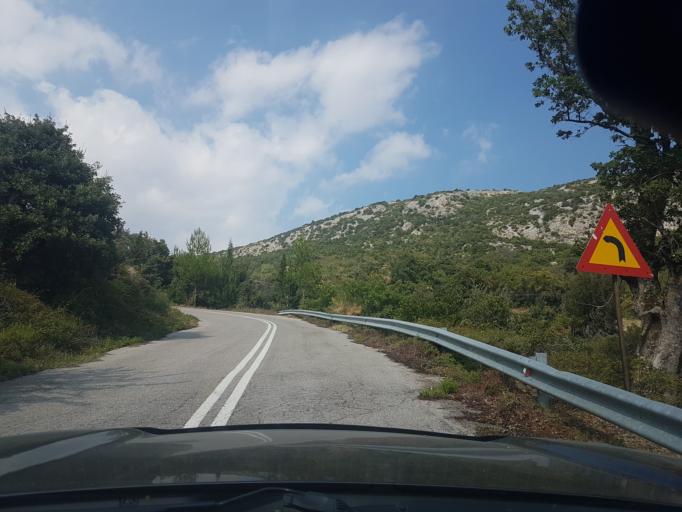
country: GR
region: Central Greece
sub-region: Nomos Evvoias
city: Yimnon
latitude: 38.5362
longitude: 23.9715
